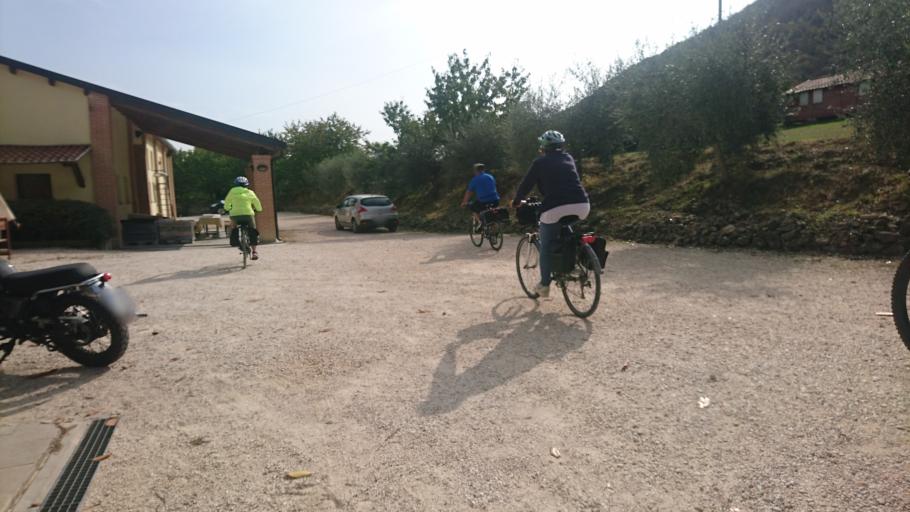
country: IT
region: Veneto
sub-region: Provincia di Padova
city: Arqua Petrarca
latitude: 45.2856
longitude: 11.7281
